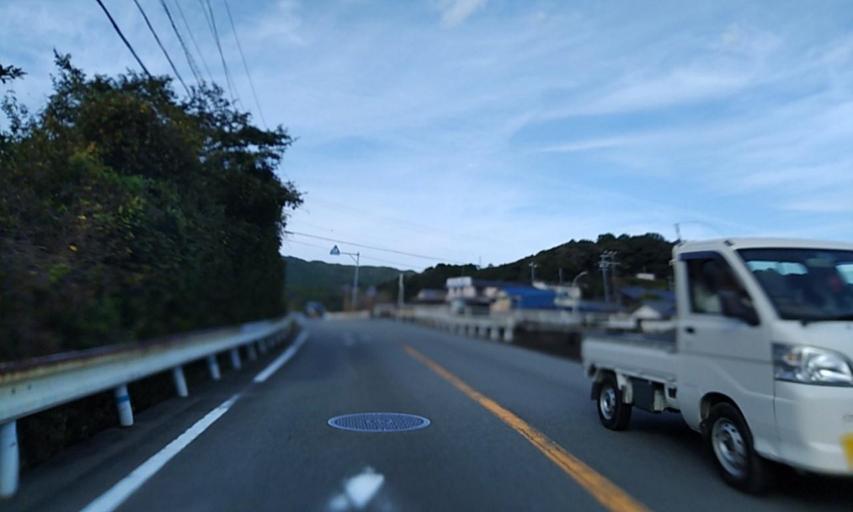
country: JP
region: Mie
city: Ise
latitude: 34.3442
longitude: 136.7312
